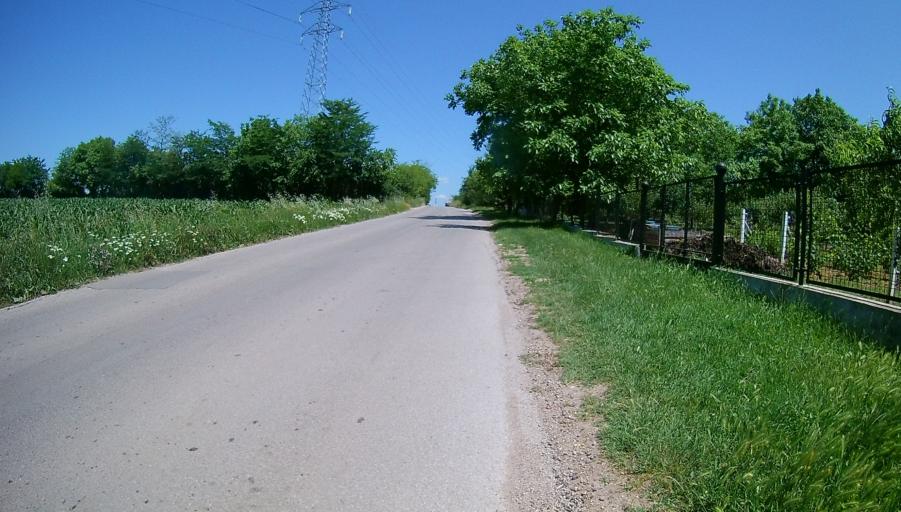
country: RS
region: Central Serbia
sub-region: Nisavski Okrug
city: Nis
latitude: 43.2963
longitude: 21.8954
